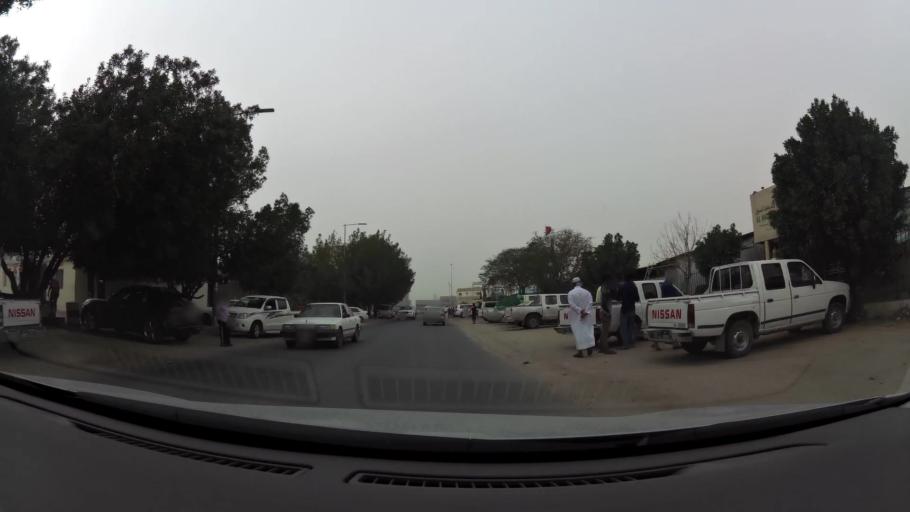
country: QA
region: Baladiyat ad Dawhah
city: Doha
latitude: 25.2491
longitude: 51.4772
